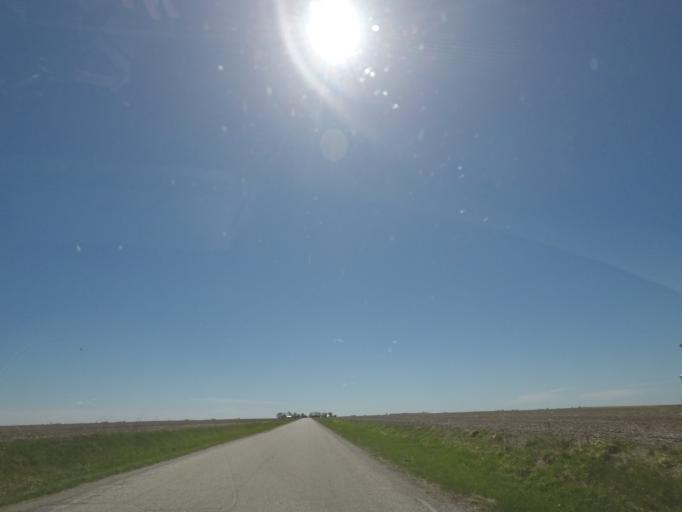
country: US
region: Illinois
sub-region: Logan County
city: Atlanta
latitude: 40.1946
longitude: -89.1941
